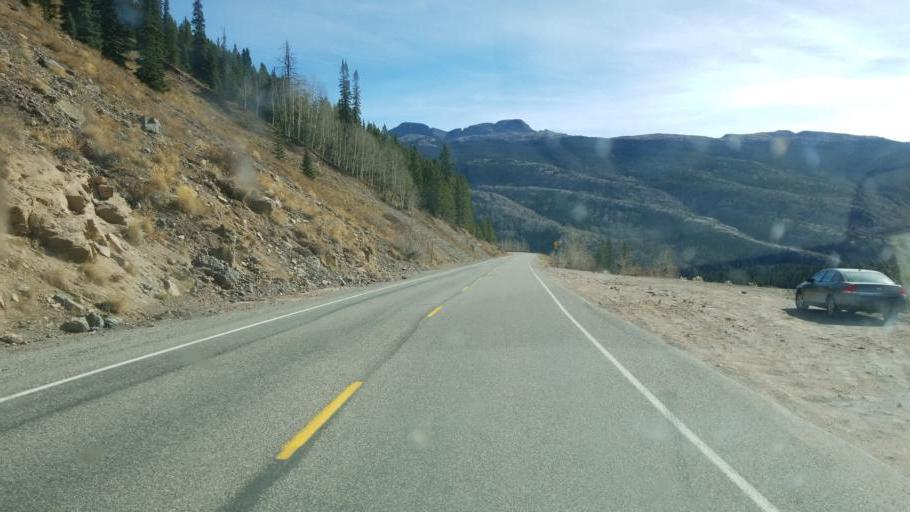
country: US
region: Colorado
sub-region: San Juan County
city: Silverton
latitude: 37.7086
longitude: -107.7705
